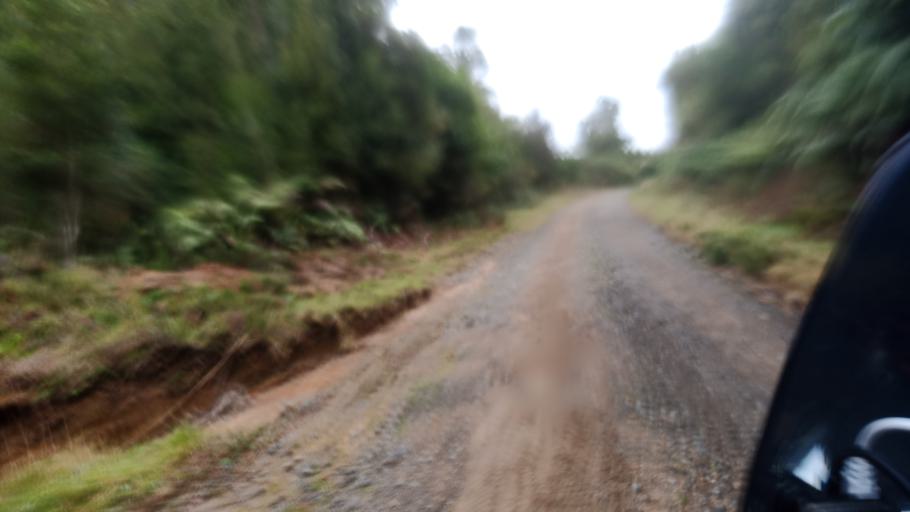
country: NZ
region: Bay of Plenty
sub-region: Whakatane District
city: Murupara
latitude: -38.6757
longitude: 176.6152
